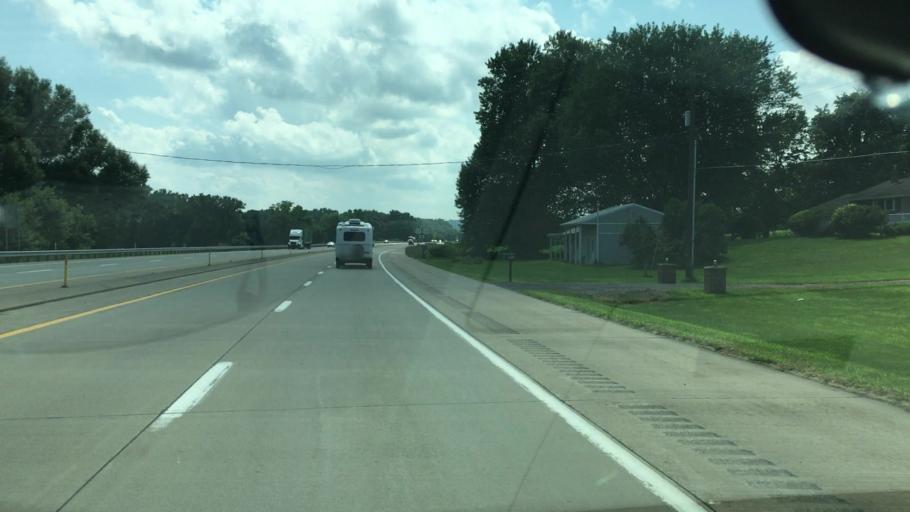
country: US
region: Pennsylvania
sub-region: Dauphin County
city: Millersburg
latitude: 40.6556
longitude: -76.9218
